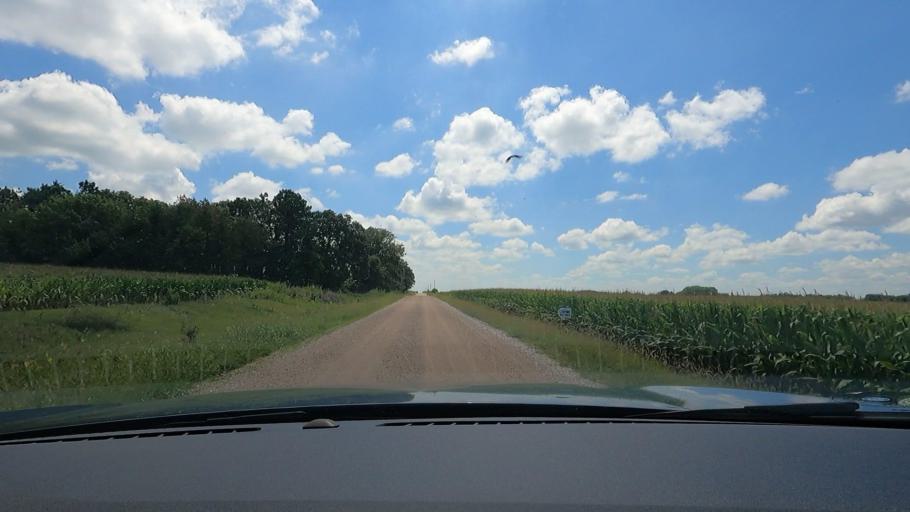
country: US
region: Nebraska
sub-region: Saunders County
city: Wahoo
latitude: 41.2663
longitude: -96.5418
